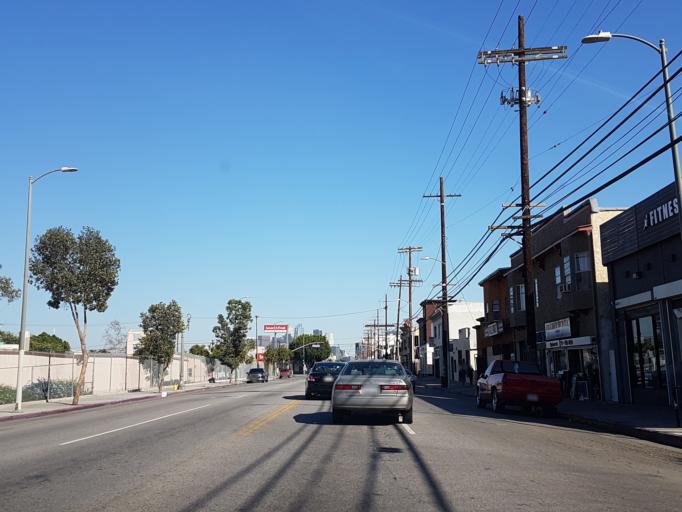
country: US
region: California
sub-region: Los Angeles County
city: Silver Lake
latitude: 34.0472
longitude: -118.3070
